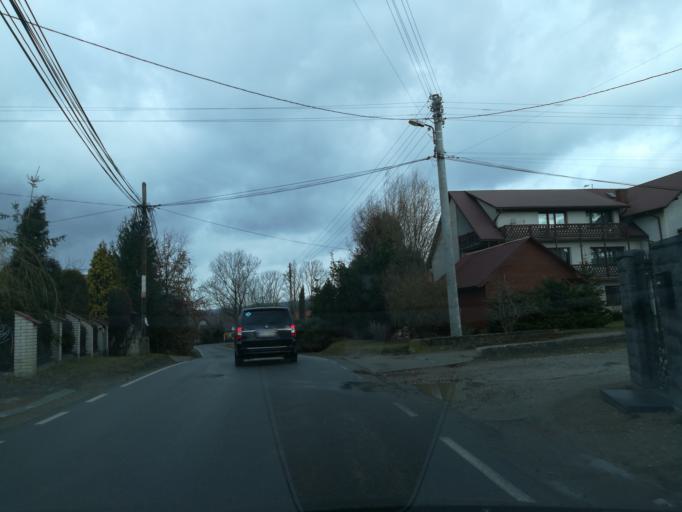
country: PL
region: Lesser Poland Voivodeship
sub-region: Krakow
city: Sidzina
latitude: 49.9832
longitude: 19.8734
